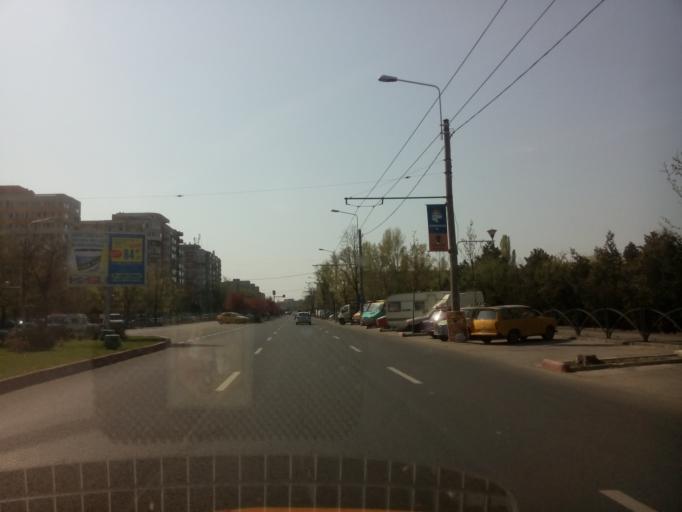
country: RO
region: Ilfov
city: Dobroesti
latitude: 44.4282
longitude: 26.1624
